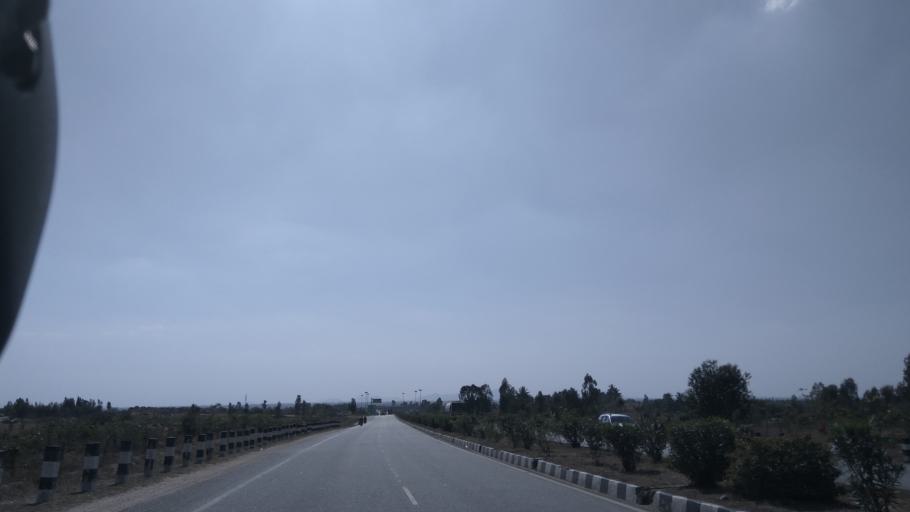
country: IN
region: Karnataka
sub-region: Kolar
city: Mulbagal
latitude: 13.1499
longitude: 78.2989
